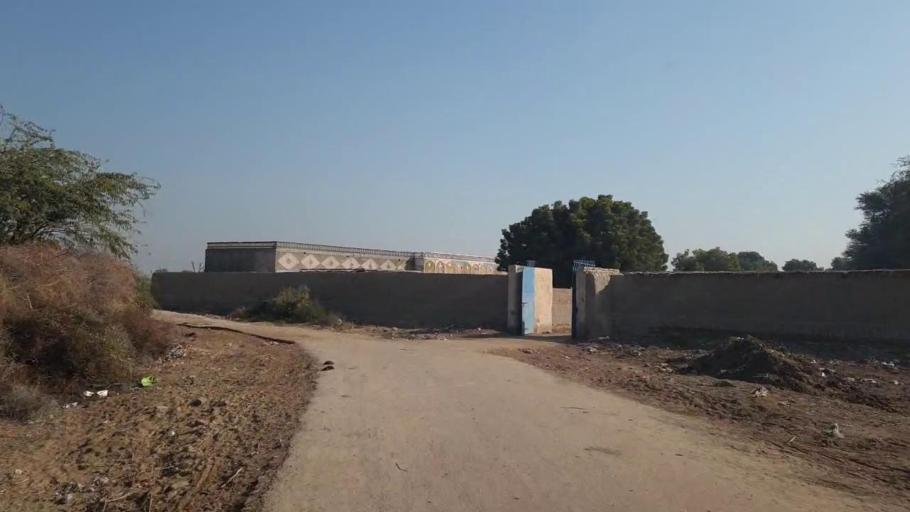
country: PK
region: Sindh
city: Shahpur Chakar
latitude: 26.0723
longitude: 68.5973
